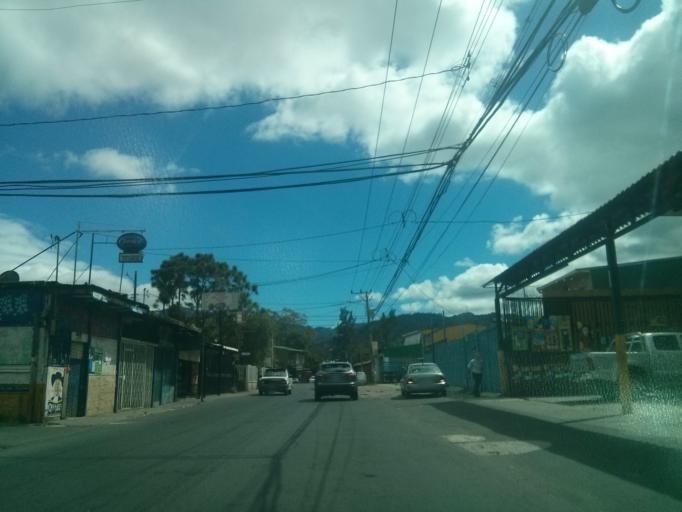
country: CR
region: San Jose
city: San Rafael Arriba
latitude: 9.8854
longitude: -84.0771
